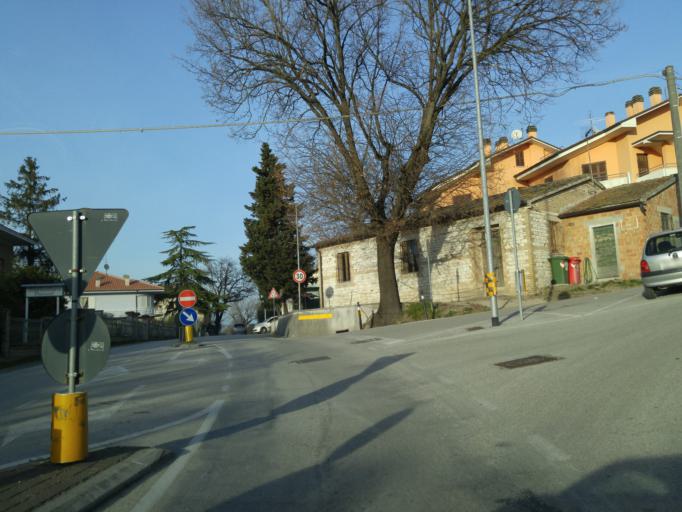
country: IT
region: The Marches
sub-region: Provincia di Pesaro e Urbino
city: Sant'Ippolito
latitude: 43.6994
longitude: 12.8672
